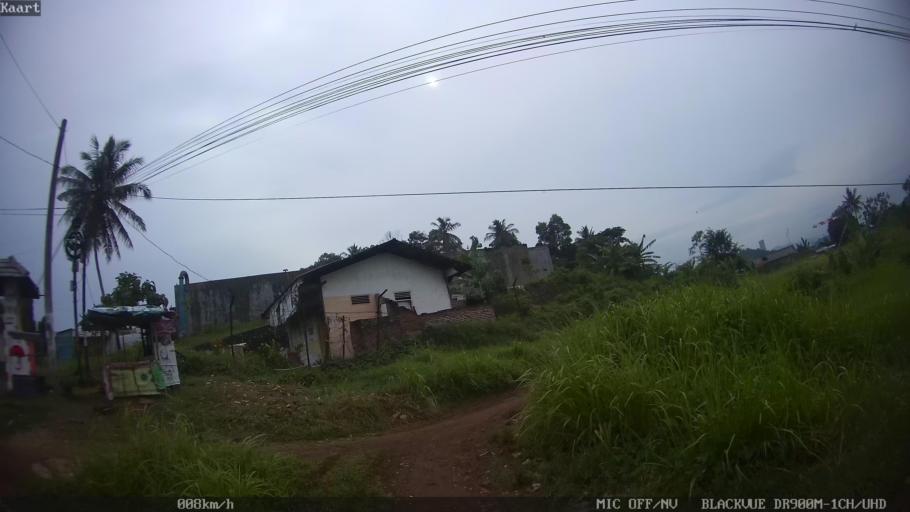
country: ID
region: Lampung
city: Kedaton
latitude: -5.4031
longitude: 105.2389
